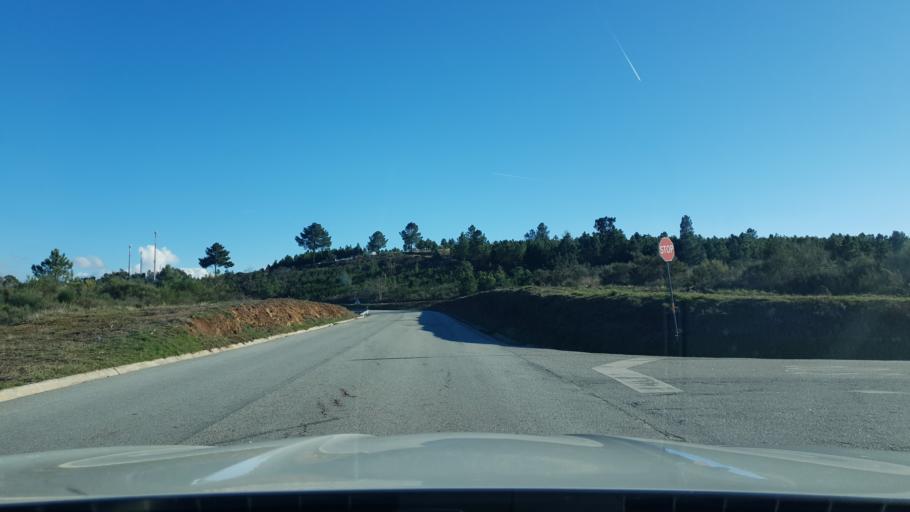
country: PT
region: Braganca
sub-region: Freixo de Espada A Cinta
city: Freixo de Espada a Cinta
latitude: 41.1193
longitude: -6.8213
